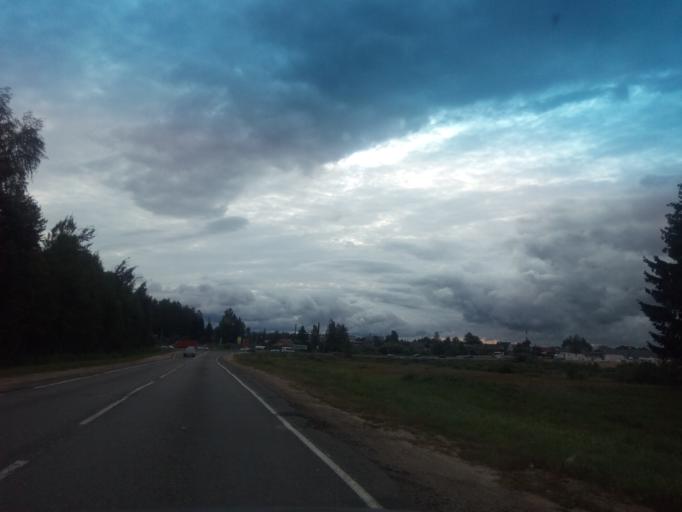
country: BY
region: Vitebsk
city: Polatsk
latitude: 55.5047
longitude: 28.7457
